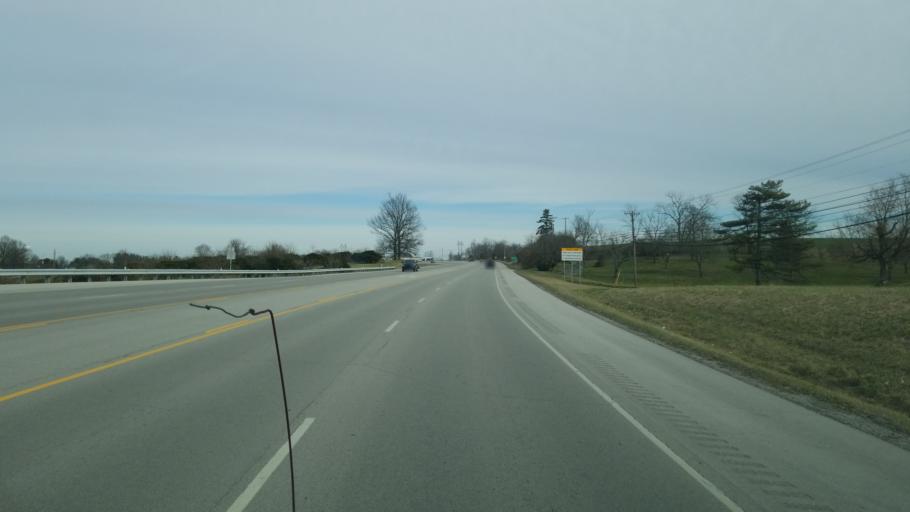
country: US
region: Ohio
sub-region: Brown County
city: Aberdeen
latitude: 38.6227
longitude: -83.8071
